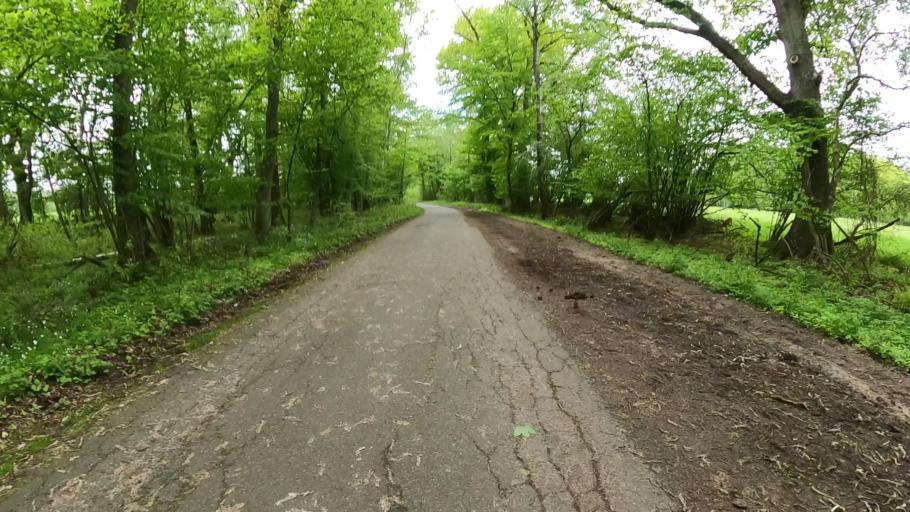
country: DE
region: Hamburg
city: Wohldorf-Ohlstedt
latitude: 53.7156
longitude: 10.1499
